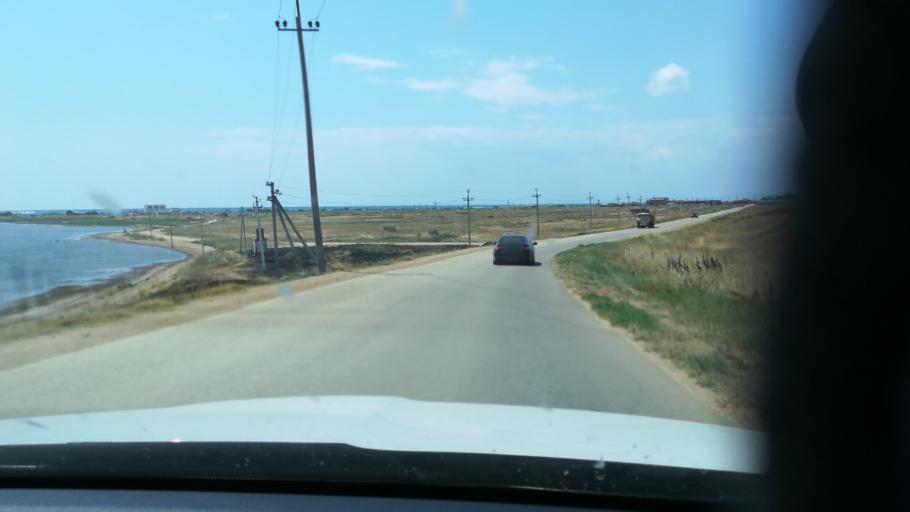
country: RU
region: Krasnodarskiy
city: Vyshestebliyevskaya
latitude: 45.1164
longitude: 36.8940
